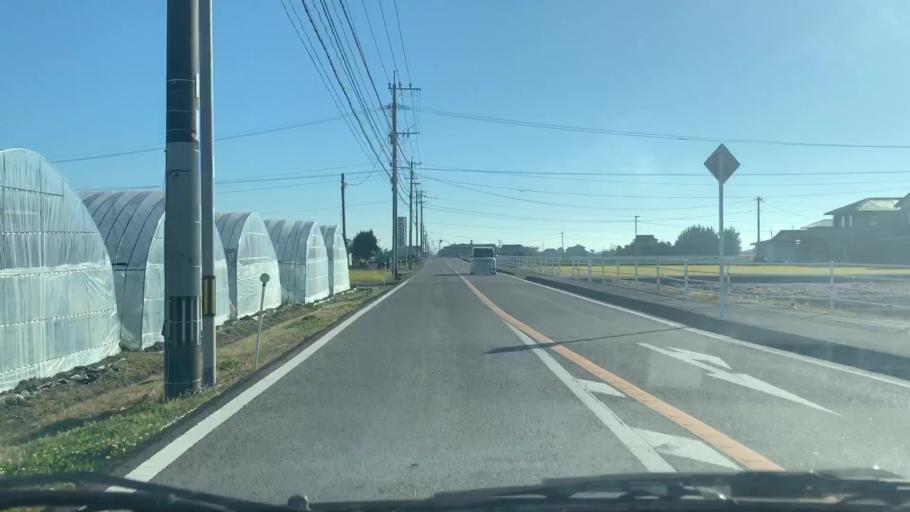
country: JP
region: Saga Prefecture
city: Kashima
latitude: 33.1848
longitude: 130.1588
